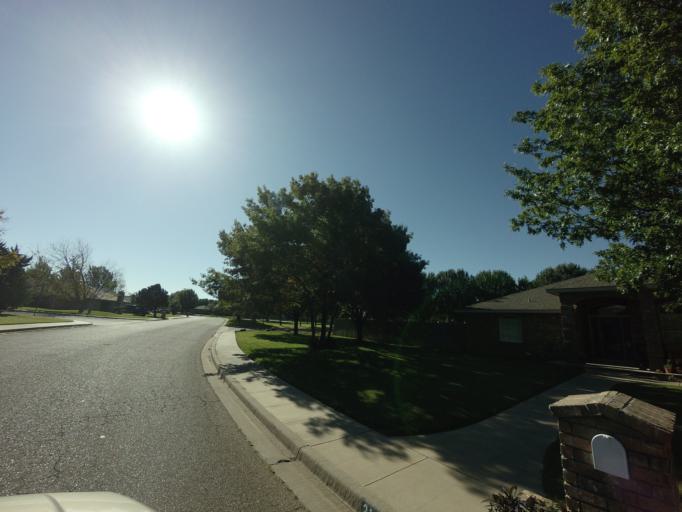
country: US
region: New Mexico
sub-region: Curry County
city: Clovis
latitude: 34.4297
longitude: -103.1765
